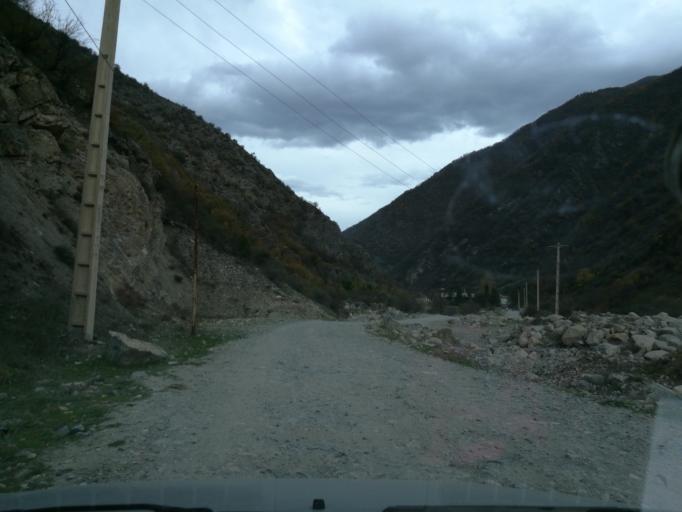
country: IR
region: Mazandaran
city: `Abbasabad
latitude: 36.4501
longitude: 51.0660
